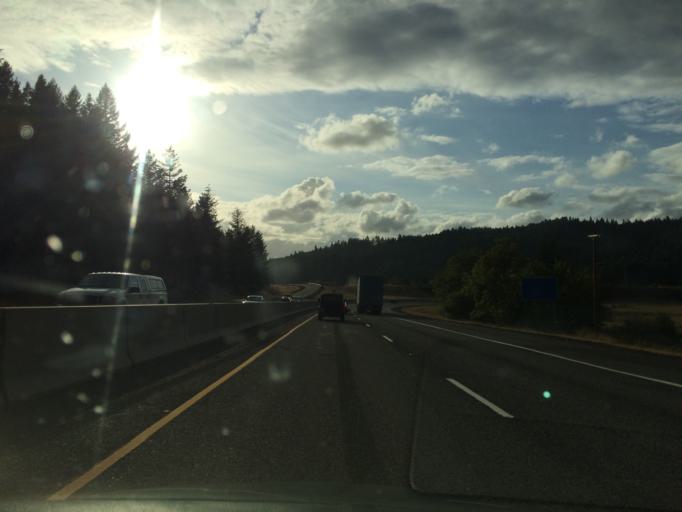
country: US
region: Oregon
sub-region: Douglas County
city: Drain
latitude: 43.7070
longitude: -123.2132
